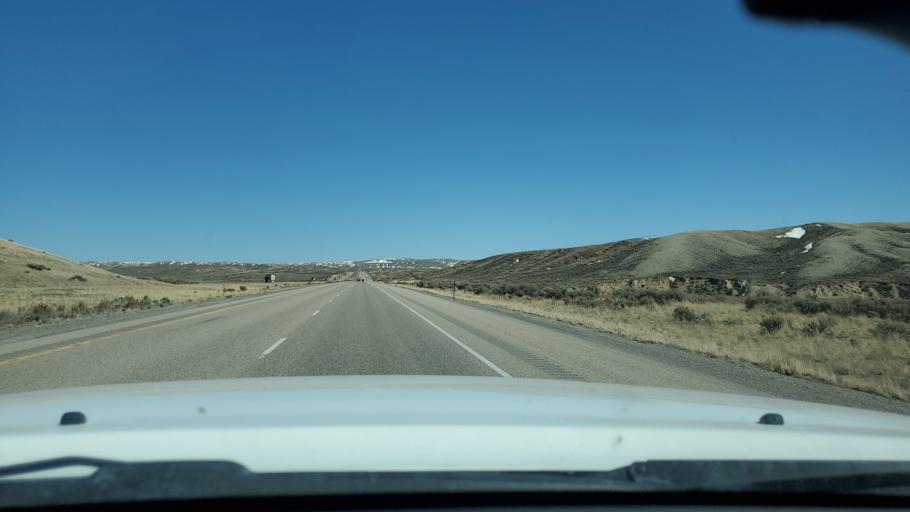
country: US
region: Wyoming
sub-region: Carbon County
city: Saratoga
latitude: 41.7360
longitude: -106.7350
